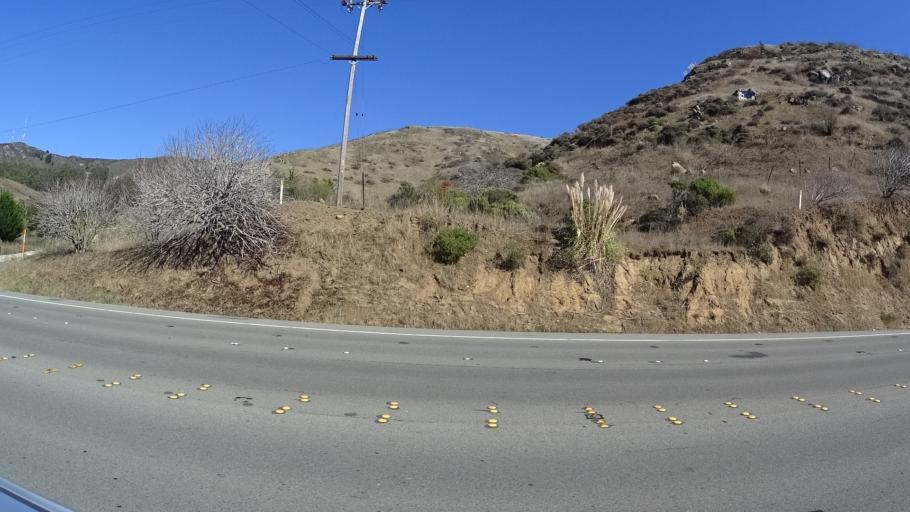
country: US
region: California
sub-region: San Mateo County
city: Colma
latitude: 37.6697
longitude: -122.4326
